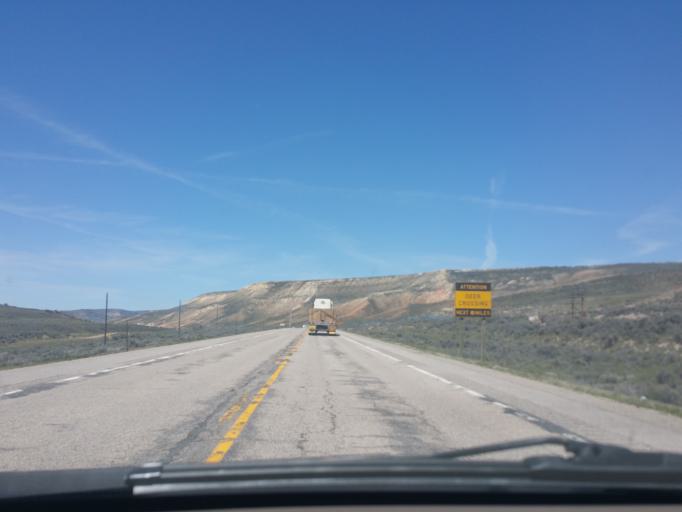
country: US
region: Wyoming
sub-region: Lincoln County
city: Kemmerer
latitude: 41.8113
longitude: -110.6213
